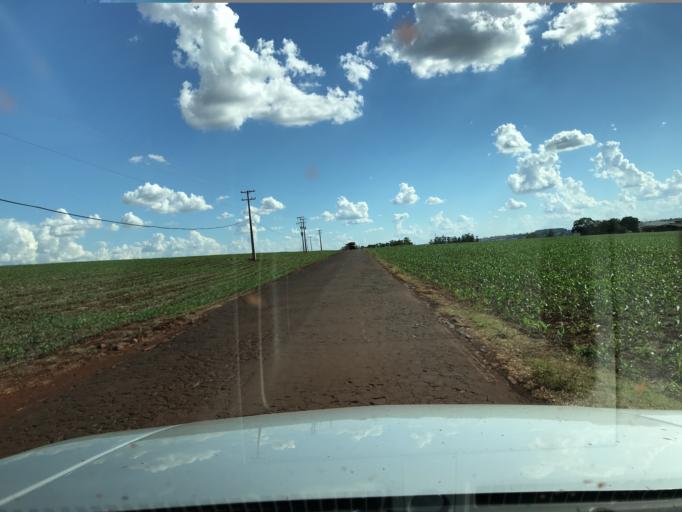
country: BR
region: Parana
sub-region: Palotina
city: Palotina
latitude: -24.2395
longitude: -53.7883
